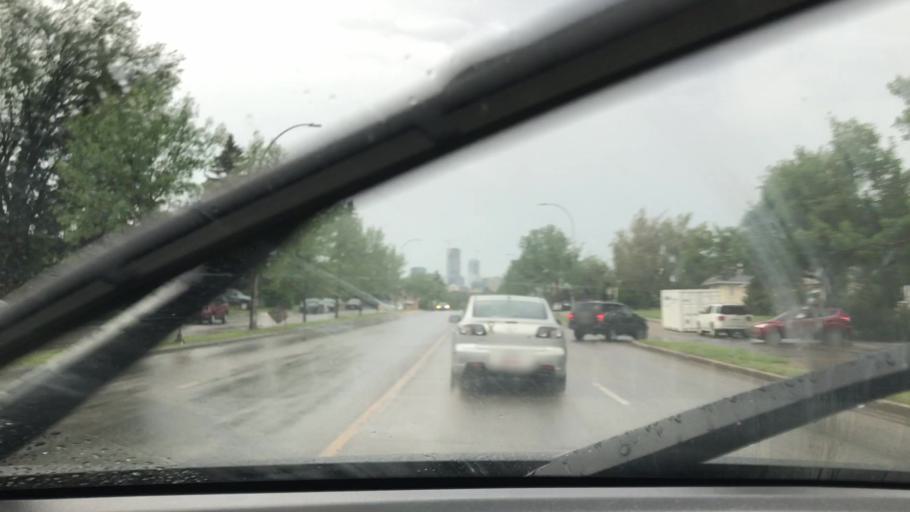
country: CA
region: Alberta
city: Edmonton
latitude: 53.5255
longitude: -113.4593
